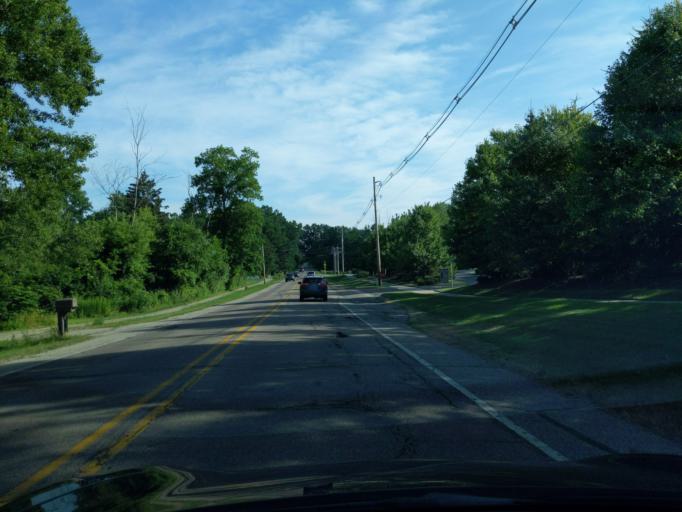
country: US
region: Michigan
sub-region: Ingham County
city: Okemos
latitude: 42.7427
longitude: -84.4277
